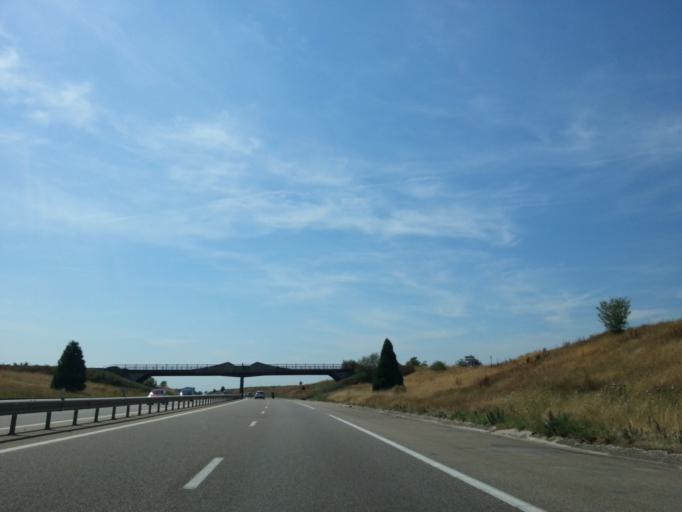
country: FR
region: Alsace
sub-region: Departement du Bas-Rhin
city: Stotzheim
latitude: 48.3976
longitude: 7.4760
